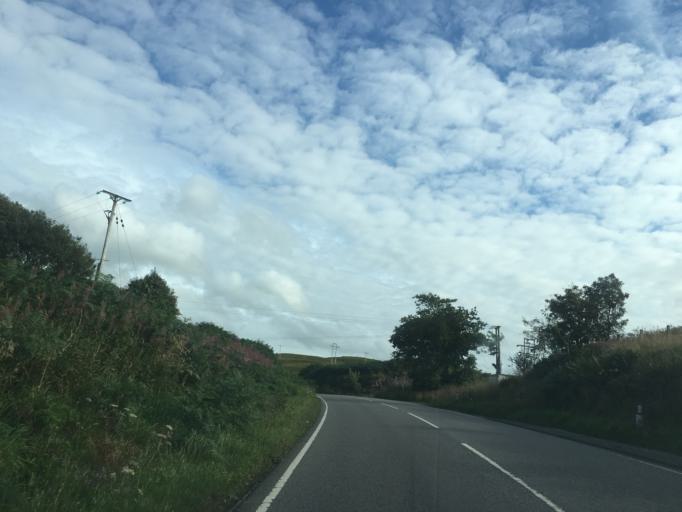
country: GB
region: Scotland
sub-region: Argyll and Bute
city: Oban
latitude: 56.3950
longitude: -5.4700
